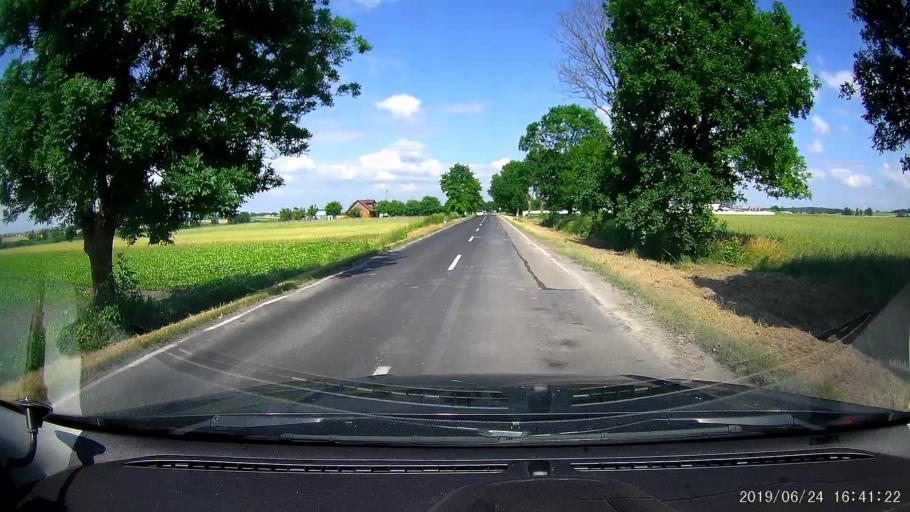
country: PL
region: Lublin Voivodeship
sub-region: Powiat tomaszowski
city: Michalow
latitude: 50.5329
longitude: 23.5971
